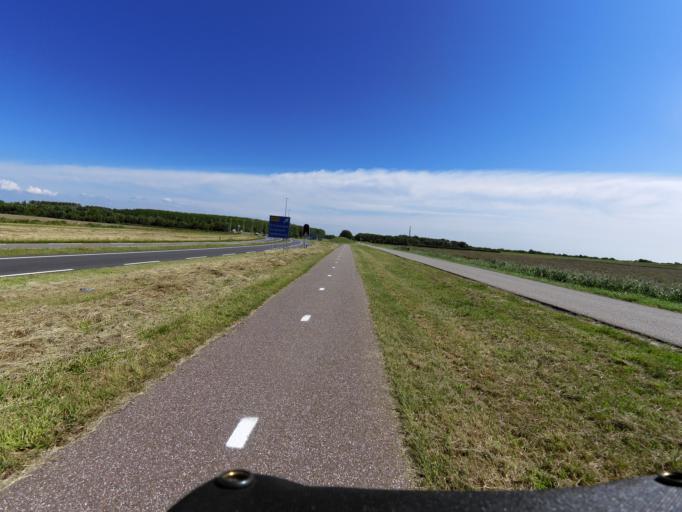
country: NL
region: South Holland
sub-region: Gemeente Goeree-Overflakkee
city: Goedereede
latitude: 51.8075
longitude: 4.0052
